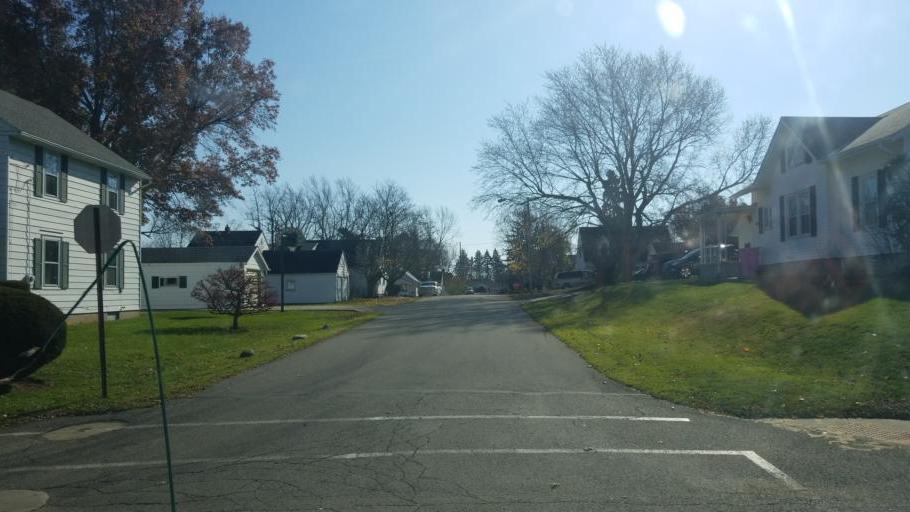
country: US
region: Ohio
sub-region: Richland County
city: Mansfield
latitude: 40.7432
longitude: -82.5188
